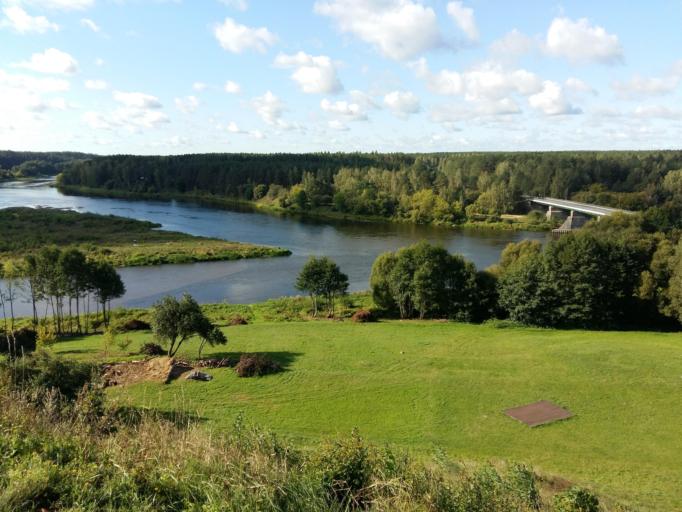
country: LT
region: Alytaus apskritis
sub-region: Alytaus rajonas
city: Daugai
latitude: 54.1594
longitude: 24.1826
